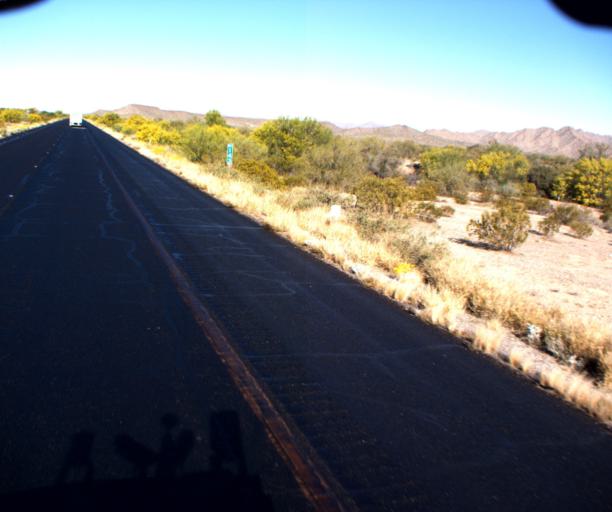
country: US
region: Arizona
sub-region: Pinal County
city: Maricopa
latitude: 32.8454
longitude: -112.2817
